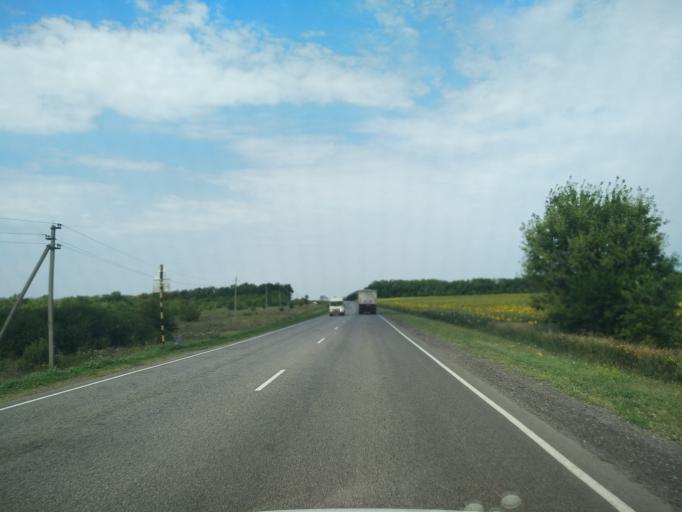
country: RU
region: Voronezj
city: Verkhnyaya Khava
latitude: 51.6783
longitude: 39.7967
